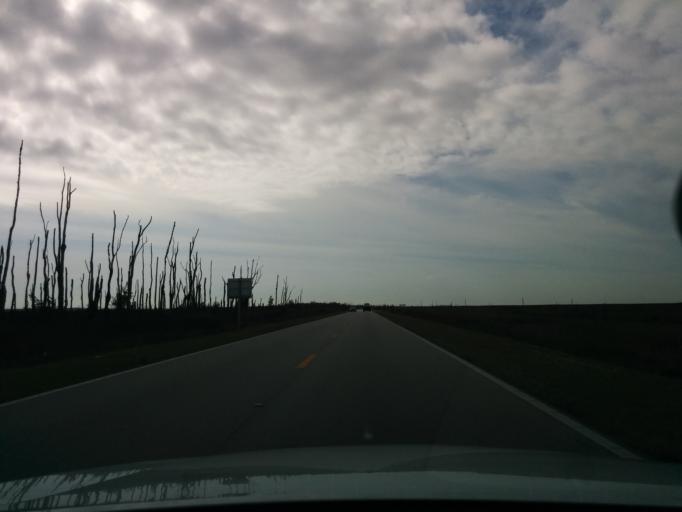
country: US
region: Florida
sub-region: Miami-Dade County
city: Tamiami
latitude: 25.8232
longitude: -80.4826
